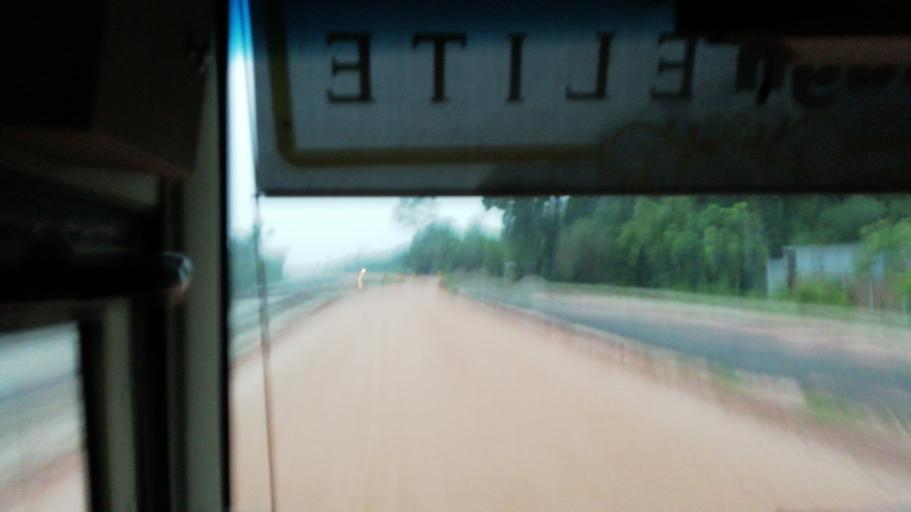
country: BD
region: Dhaka
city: Char Bhadrasan
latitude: 23.4004
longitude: 90.1317
